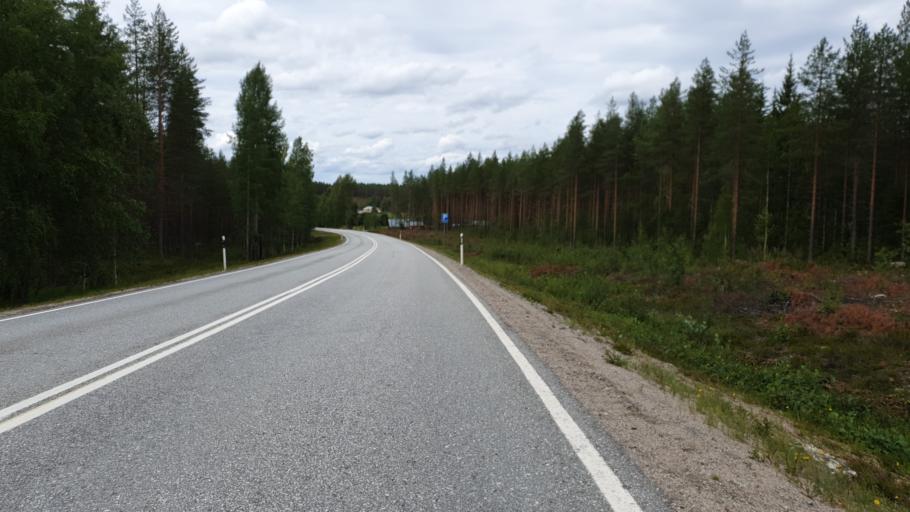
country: FI
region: Kainuu
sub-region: Kehys-Kainuu
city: Kuhmo
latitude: 64.4906
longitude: 29.8193
